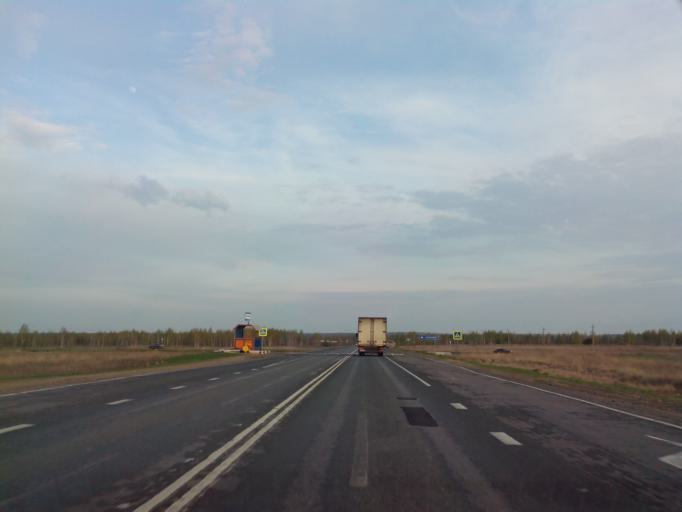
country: RU
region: Rjazan
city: Korablino
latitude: 53.7363
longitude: 39.8944
